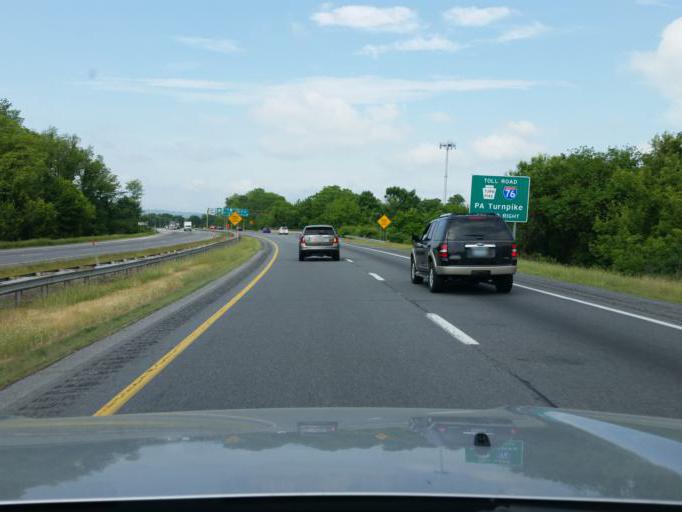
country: US
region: Pennsylvania
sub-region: Dauphin County
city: Highspire
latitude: 40.2230
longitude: -76.7812
